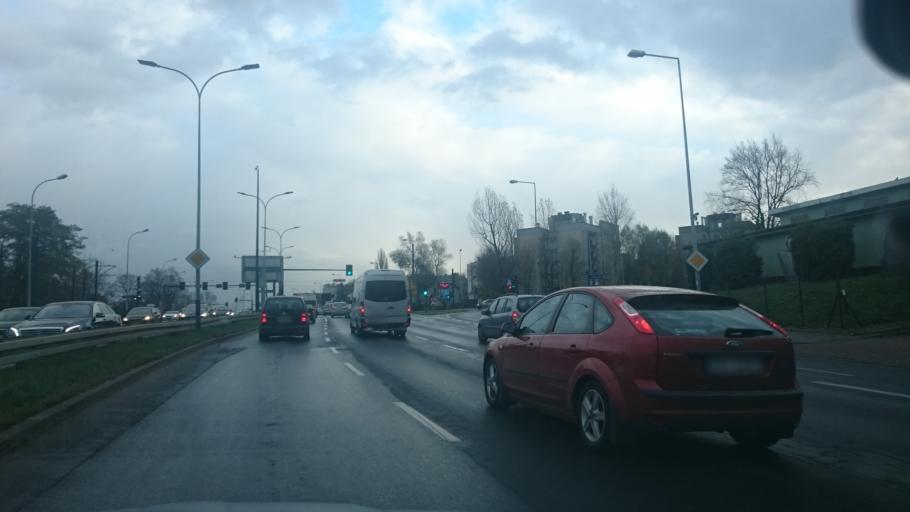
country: PL
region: Lesser Poland Voivodeship
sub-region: Krakow
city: Krakow
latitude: 50.0247
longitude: 19.9787
